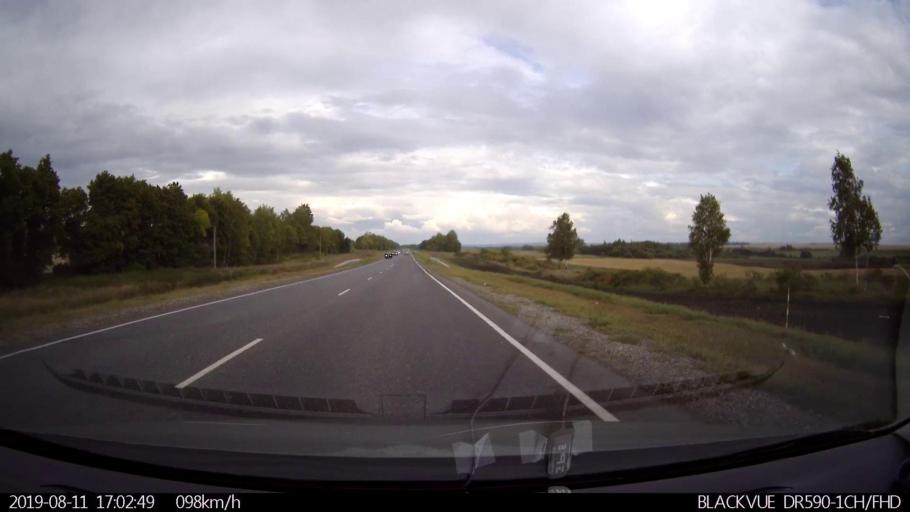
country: RU
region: Ulyanovsk
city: Mayna
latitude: 54.3049
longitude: 47.7237
